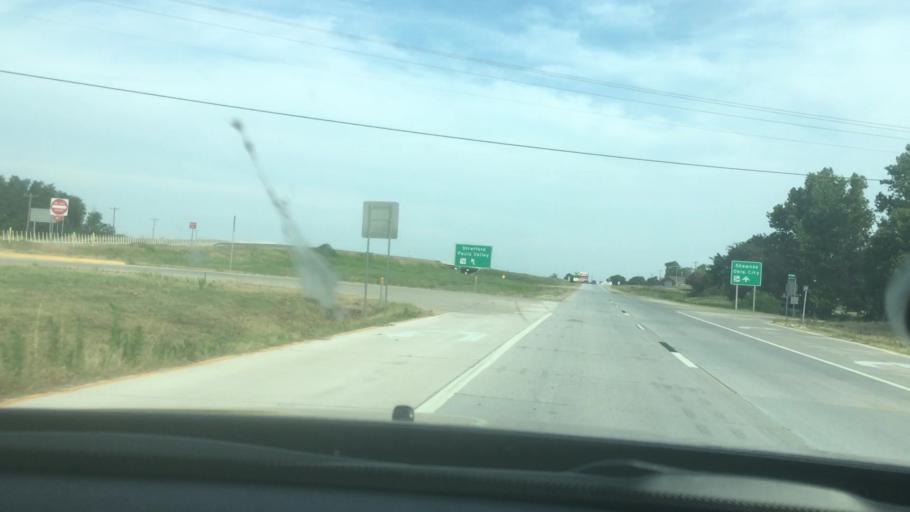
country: US
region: Oklahoma
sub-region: Pontotoc County
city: Ada
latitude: 34.7840
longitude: -96.7215
